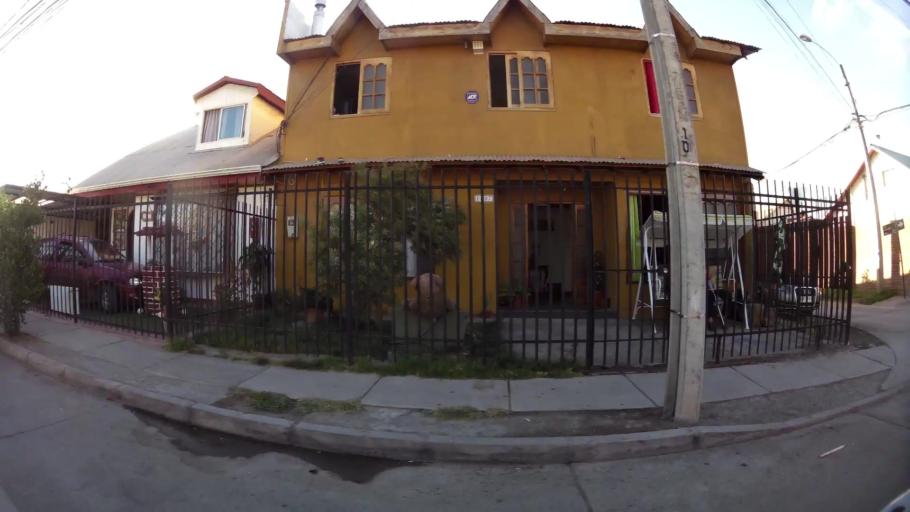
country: CL
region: O'Higgins
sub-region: Provincia de Cachapoal
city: Rancagua
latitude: -34.1749
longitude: -70.7655
